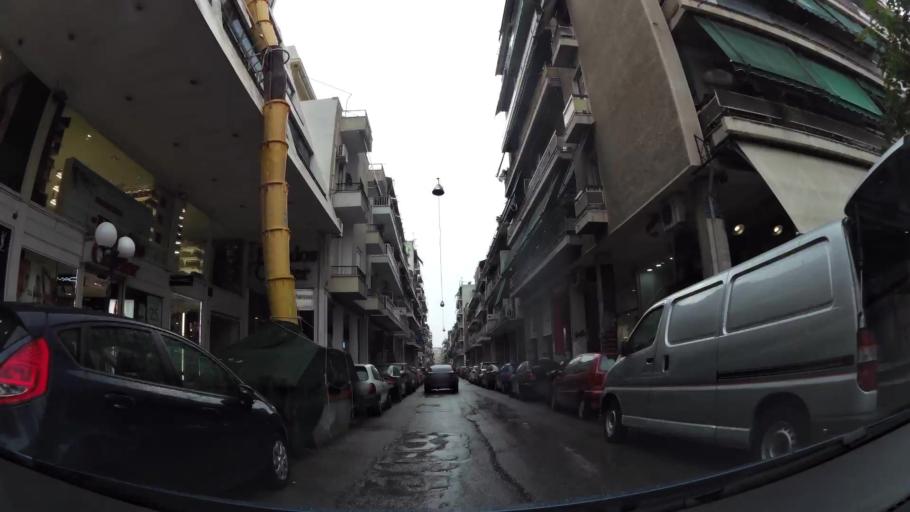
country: GR
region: Attica
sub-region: Nomarchia Athinas
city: Vyronas
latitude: 37.9648
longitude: 23.7509
